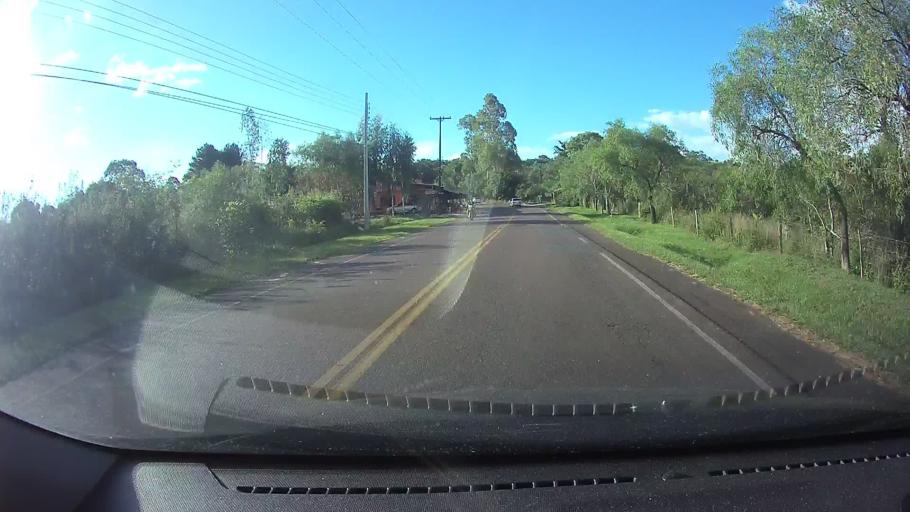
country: PY
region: Cordillera
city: Altos
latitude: -25.1879
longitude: -57.2249
